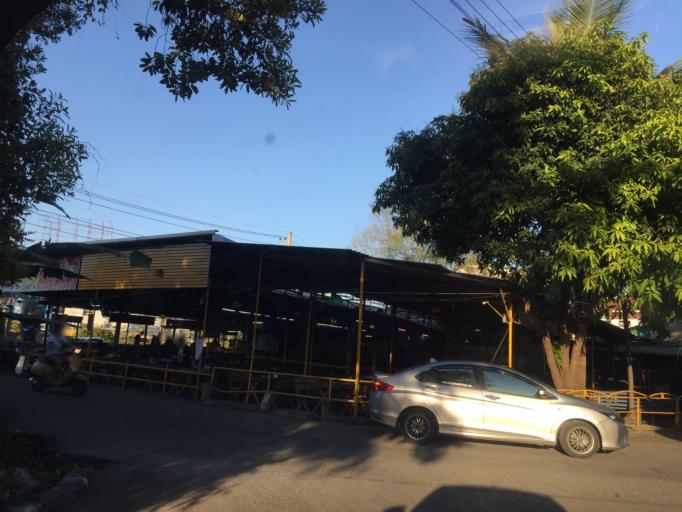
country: TH
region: Chiang Mai
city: Chiang Mai
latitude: 18.8108
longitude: 98.9806
